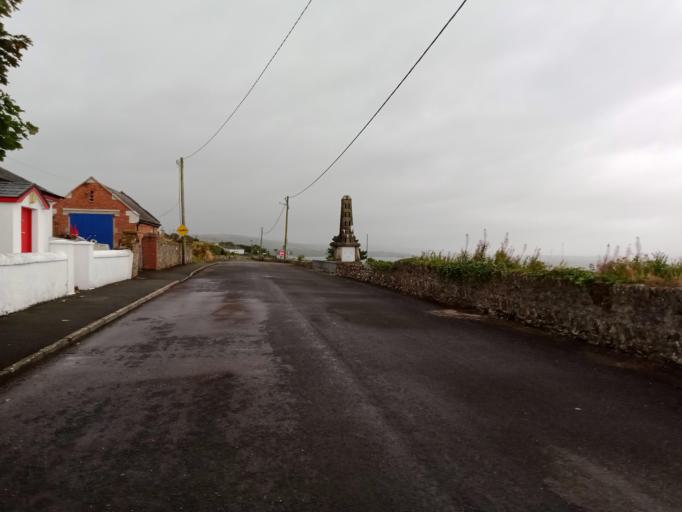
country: IE
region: Munster
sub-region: Waterford
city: Dungarvan
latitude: 52.0539
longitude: -7.5453
